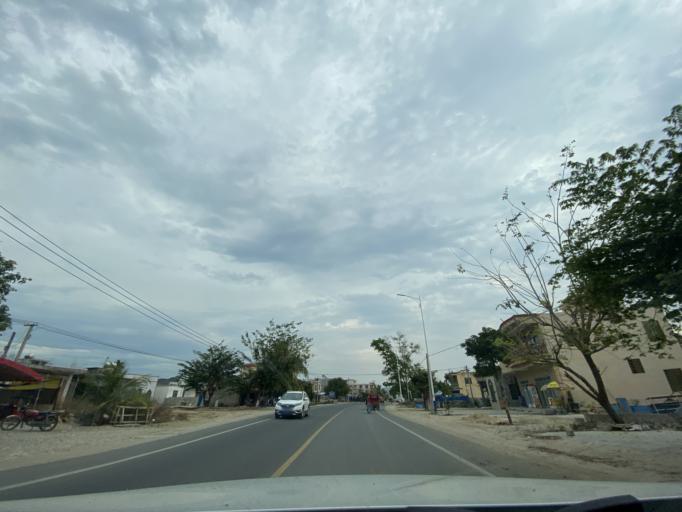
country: CN
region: Hainan
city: Yingzhou
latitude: 18.4239
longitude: 109.8221
